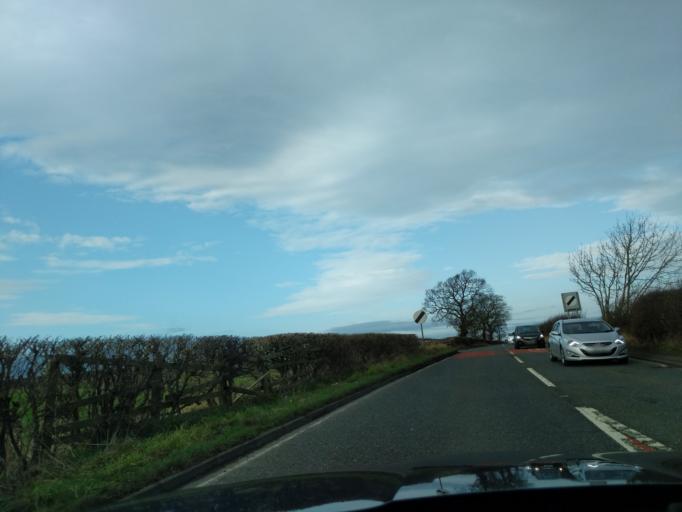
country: GB
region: England
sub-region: Northumberland
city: Ponteland
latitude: 55.0504
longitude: -1.7566
